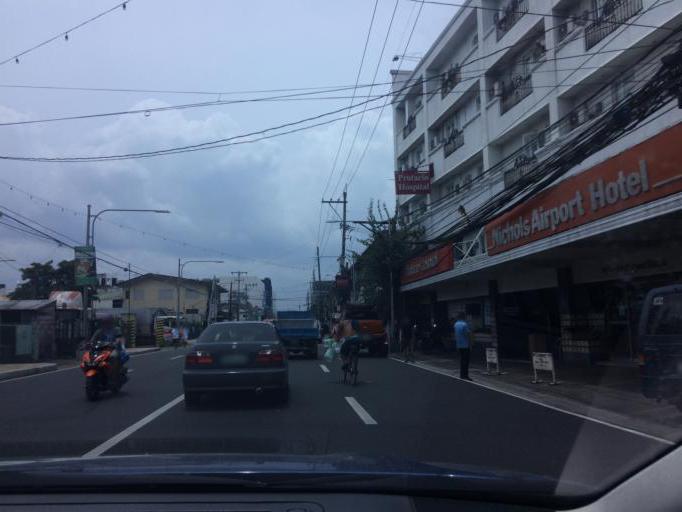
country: PH
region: Metro Manila
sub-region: Makati City
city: Makati City
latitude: 14.5245
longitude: 120.9970
